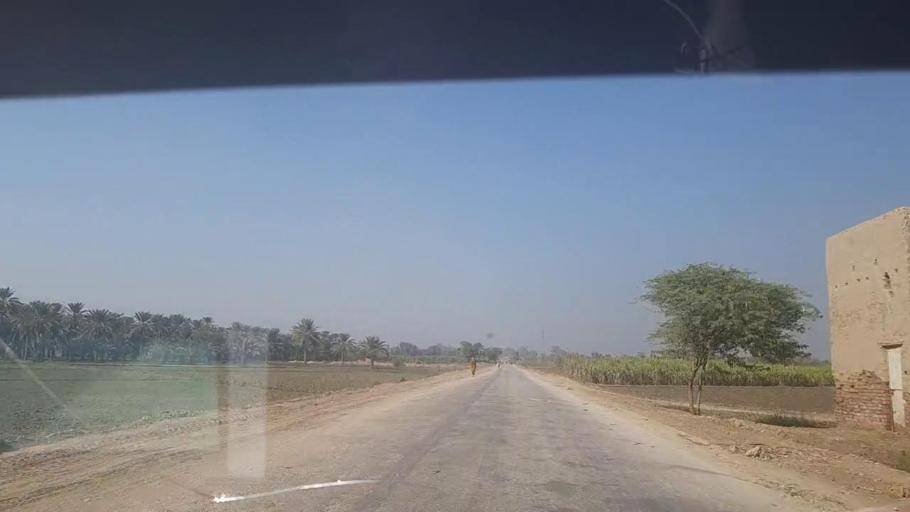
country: PK
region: Sindh
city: Kot Diji
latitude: 27.4244
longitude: 68.6577
